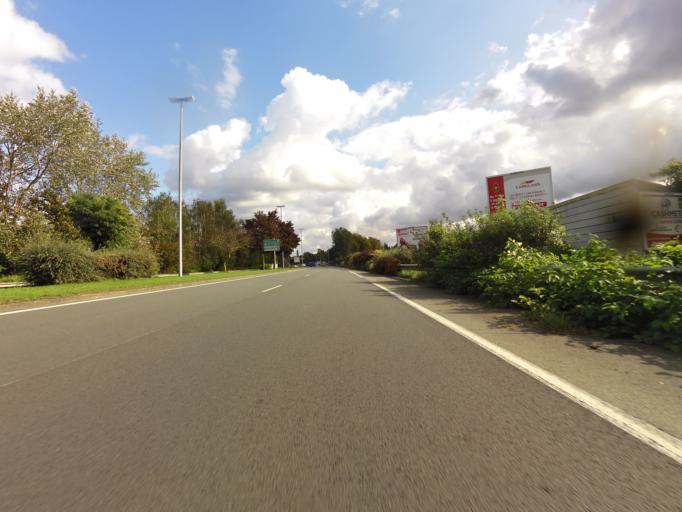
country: FR
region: Nord-Pas-de-Calais
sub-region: Departement du Nord
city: Proville
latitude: 50.1749
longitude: 3.2124
